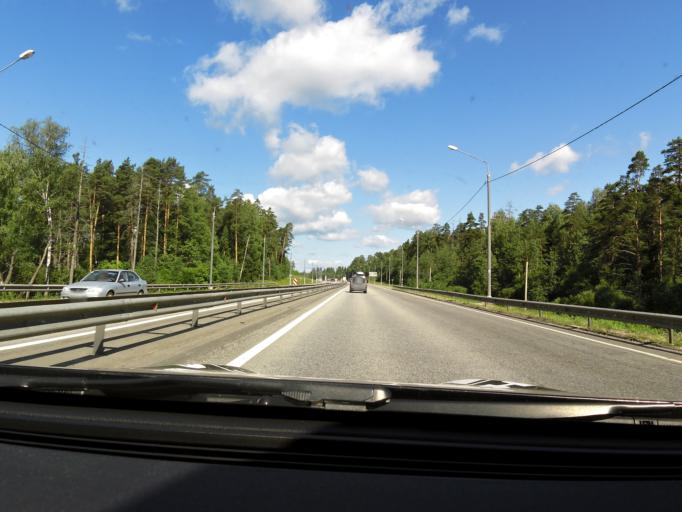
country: RU
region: Tverskaya
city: Likhoslavl'
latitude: 56.9400
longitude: 35.5093
